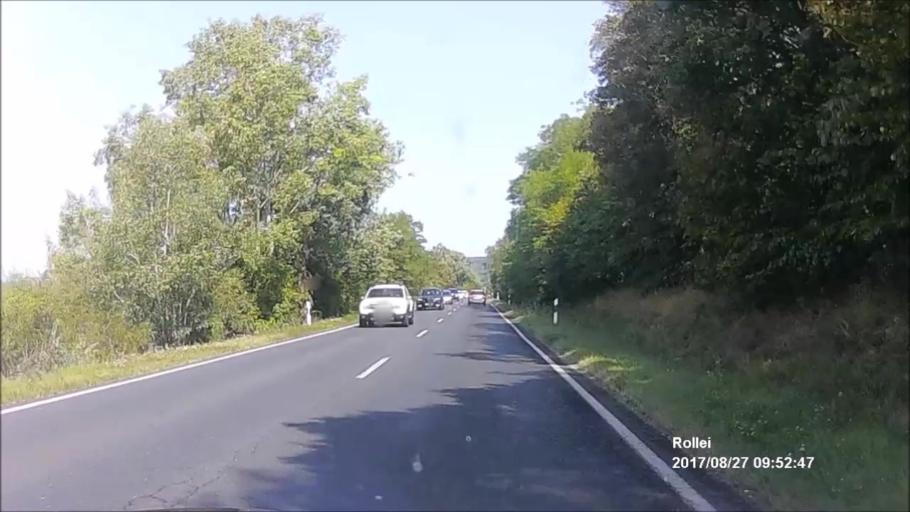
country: HU
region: Gyor-Moson-Sopron
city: Sopron
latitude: 47.7074
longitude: 16.5757
